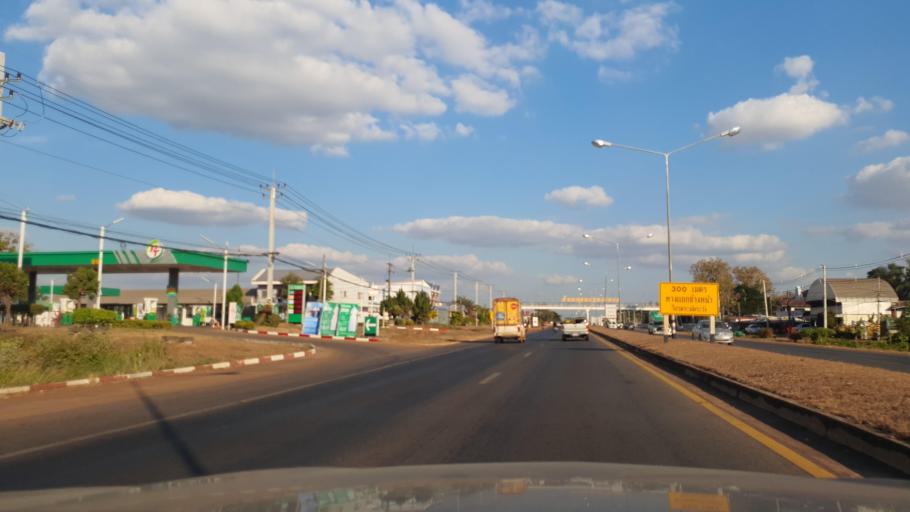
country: TH
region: Sakon Nakhon
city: Sakon Nakhon
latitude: 17.2568
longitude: 104.1700
